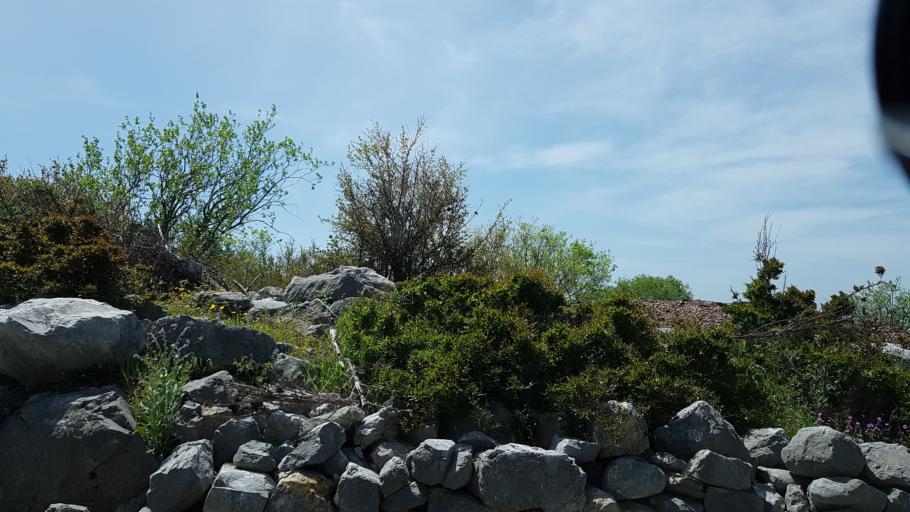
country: AL
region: Shkoder
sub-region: Rrethi i Shkodres
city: Guri i Zi
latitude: 42.1238
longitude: 19.6131
